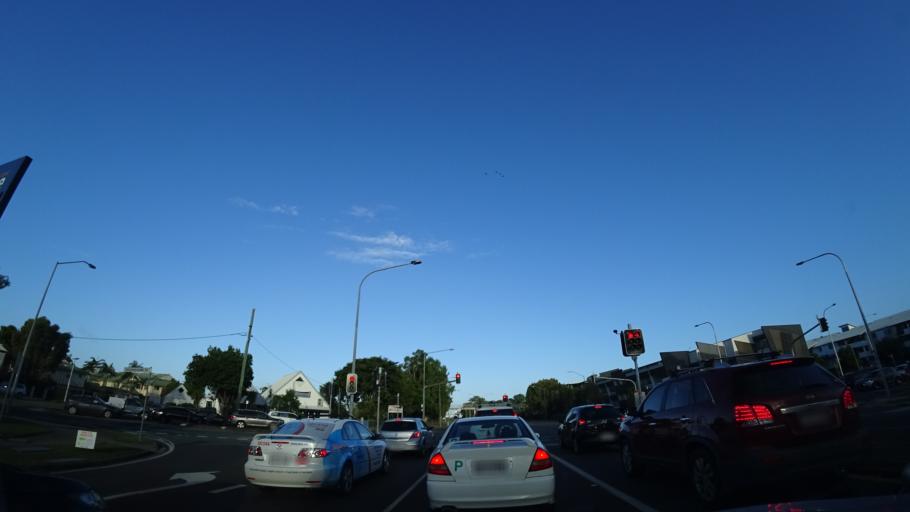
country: AU
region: Queensland
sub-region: Sunshine Coast
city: Buderim
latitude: -26.6520
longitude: 153.0824
